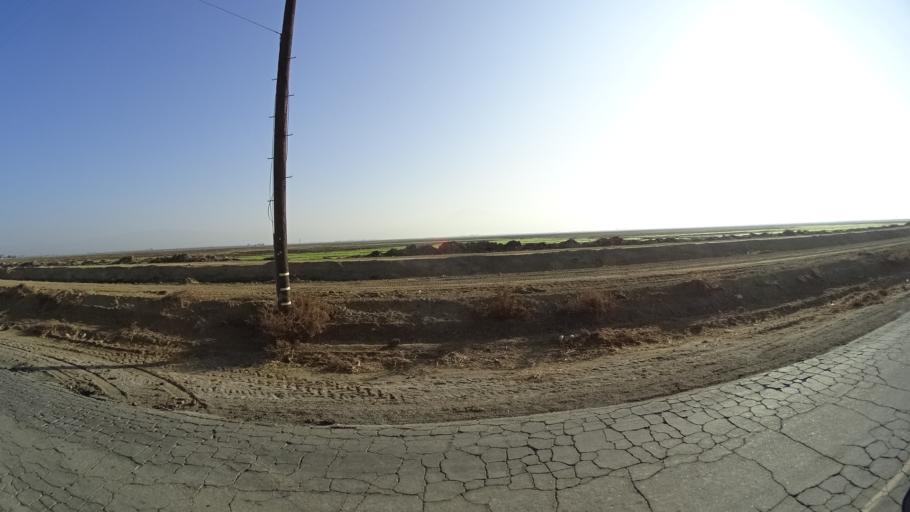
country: US
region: California
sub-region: Kern County
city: Greenfield
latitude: 35.2299
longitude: -118.9677
